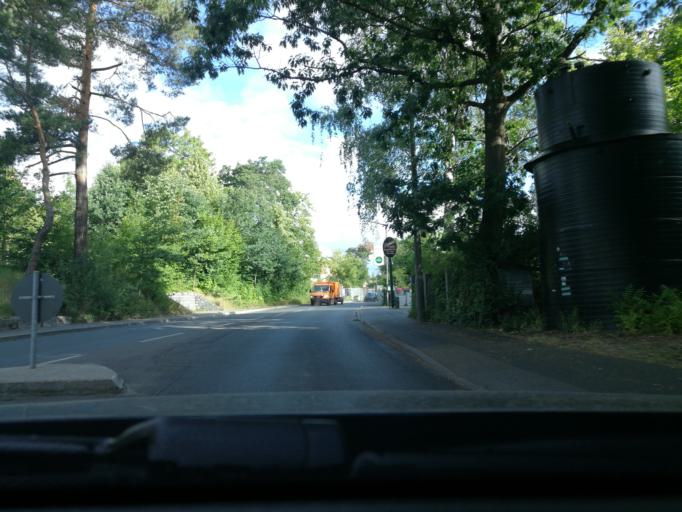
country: DE
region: Bavaria
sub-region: Regierungsbezirk Mittelfranken
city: Furth
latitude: 49.5018
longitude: 10.9683
